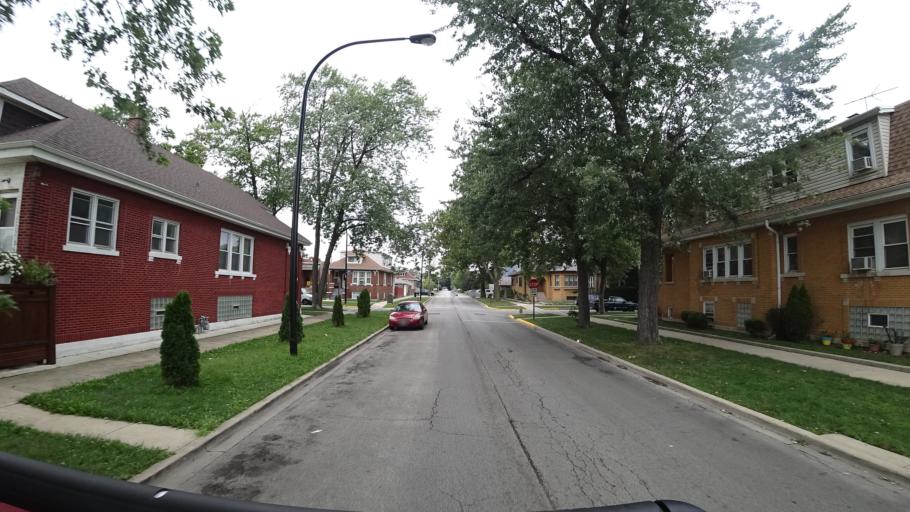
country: US
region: Illinois
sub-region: Cook County
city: Cicero
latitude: 41.8545
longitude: -87.7711
